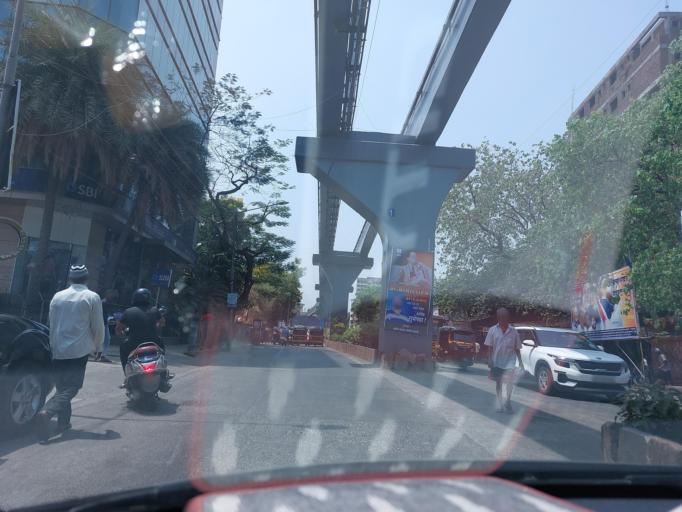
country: IN
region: Maharashtra
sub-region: Mumbai Suburban
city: Mumbai
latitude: 19.0555
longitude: 72.8950
